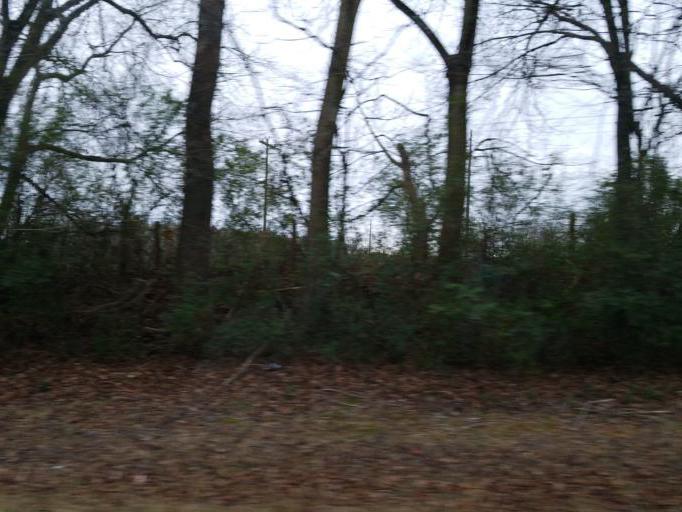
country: US
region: Georgia
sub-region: Dawson County
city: Dawsonville
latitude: 34.4876
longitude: -84.1729
